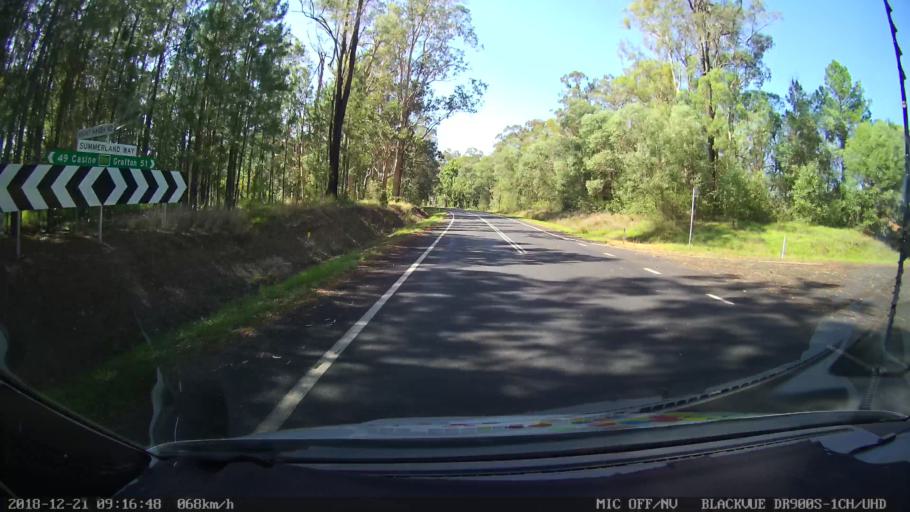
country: AU
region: New South Wales
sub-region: Clarence Valley
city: Maclean
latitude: -29.2856
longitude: 152.9888
